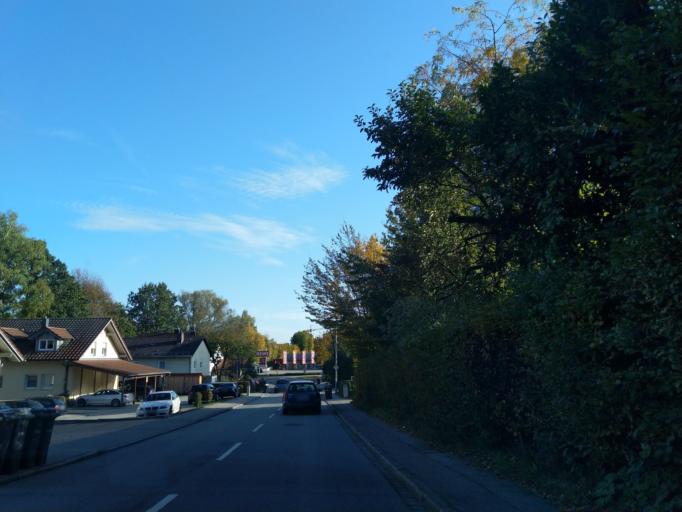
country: DE
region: Bavaria
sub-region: Lower Bavaria
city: Deggendorf
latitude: 48.8471
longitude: 12.9498
